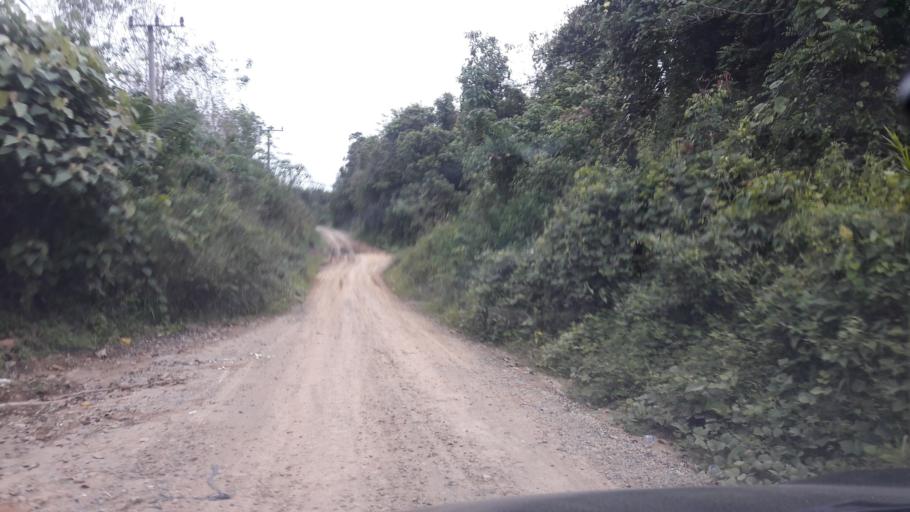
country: ID
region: South Sumatra
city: Gunungmenang
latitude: -3.1911
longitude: 103.8056
